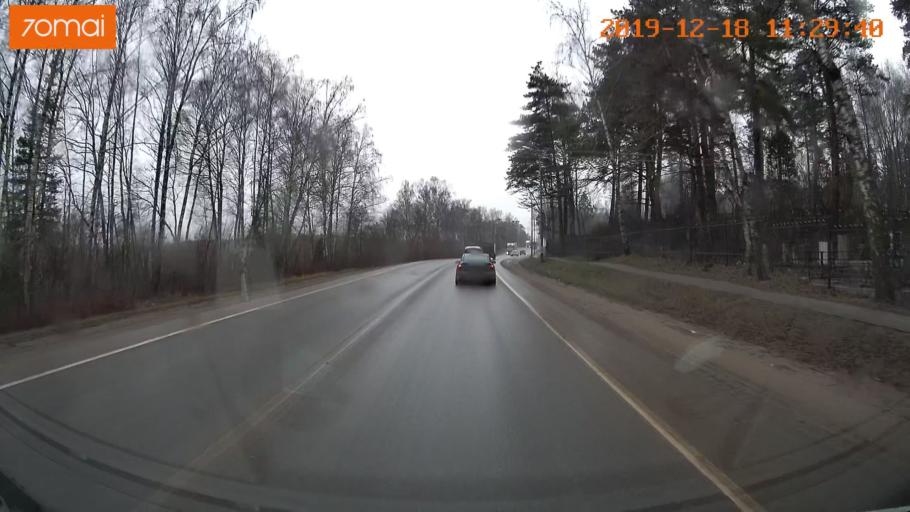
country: RU
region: Moskovskaya
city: Bol'shiye Vyazemy
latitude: 55.6514
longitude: 36.9708
